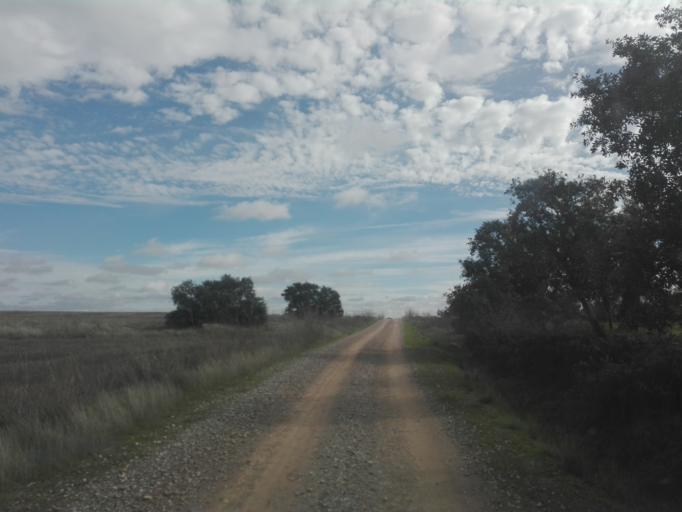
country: ES
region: Extremadura
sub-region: Provincia de Badajoz
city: Villagarcia de la Torre
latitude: 38.2927
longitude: -6.0909
